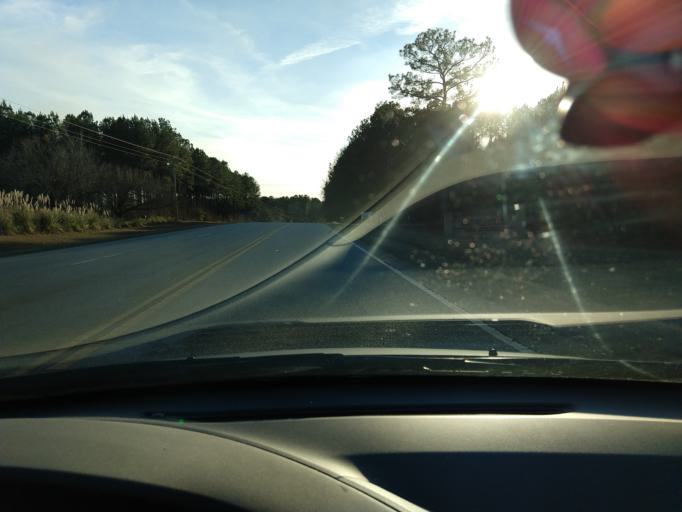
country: US
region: Georgia
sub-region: Sumter County
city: Americus
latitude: 32.1059
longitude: -84.1778
